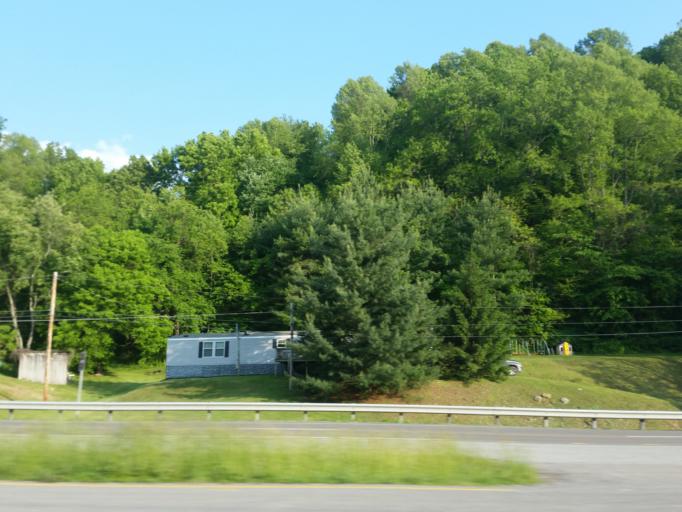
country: US
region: Virginia
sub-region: Russell County
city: Lebanon
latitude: 36.9243
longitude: -81.9995
